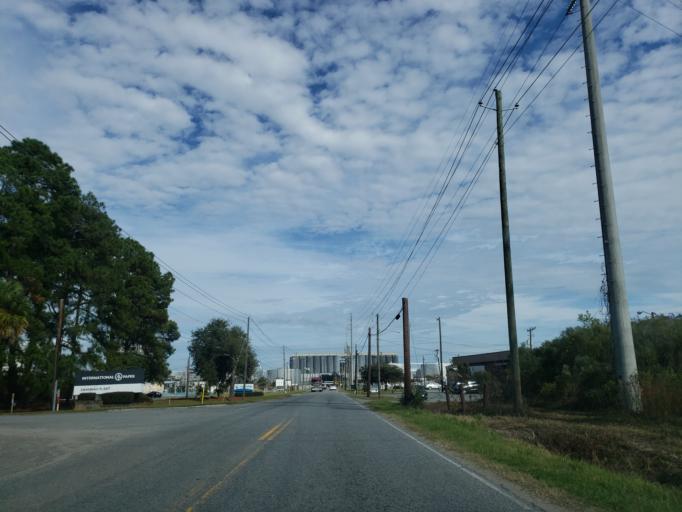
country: US
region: Georgia
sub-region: Chatham County
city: Savannah
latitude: 32.0960
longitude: -81.1237
